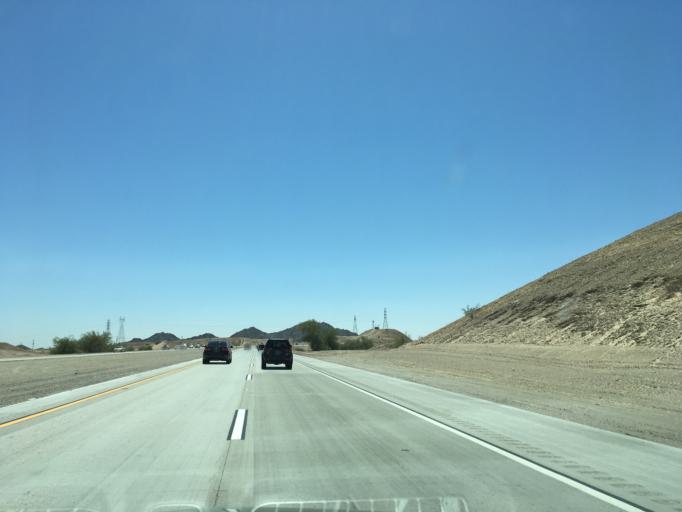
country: MX
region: Baja California
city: Los Algodones
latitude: 32.7458
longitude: -114.7053
